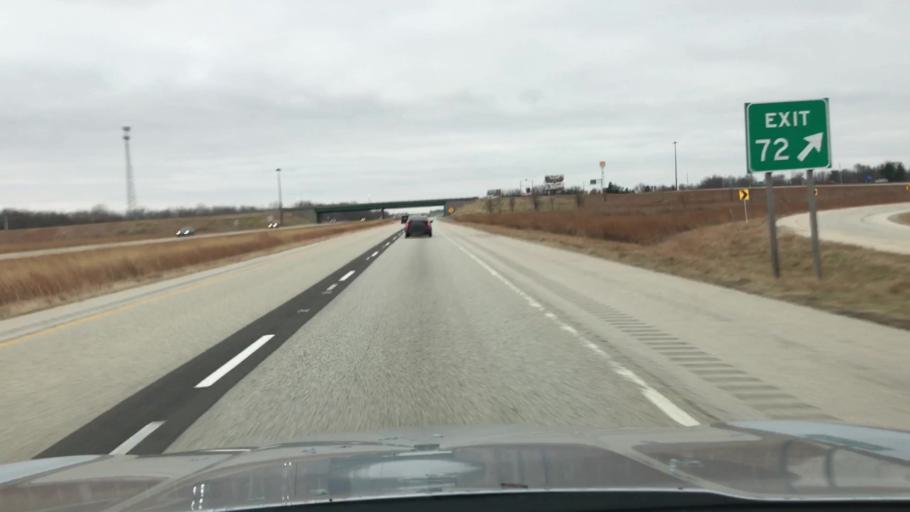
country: US
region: Illinois
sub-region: Sangamon County
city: Divernon
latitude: 39.4485
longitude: -89.6444
